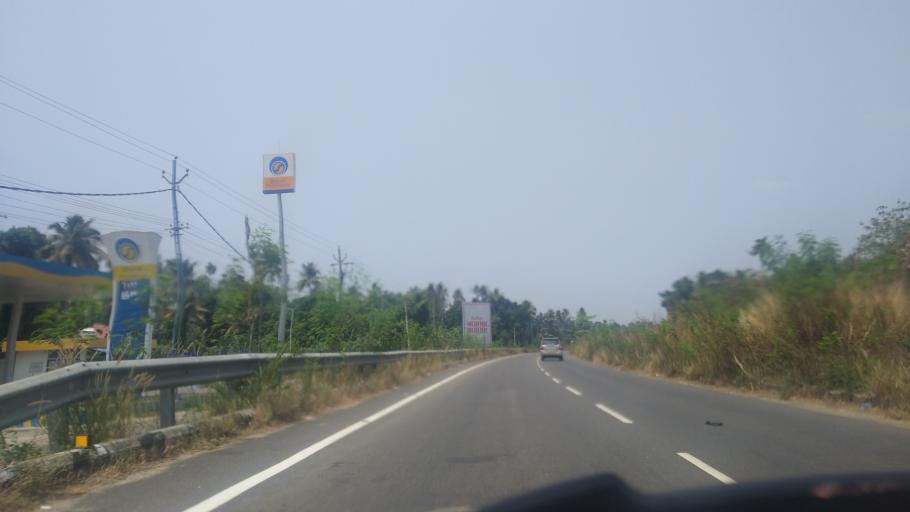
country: IN
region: Kerala
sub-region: Thrissur District
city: Kodungallur
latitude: 10.2170
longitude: 76.1966
